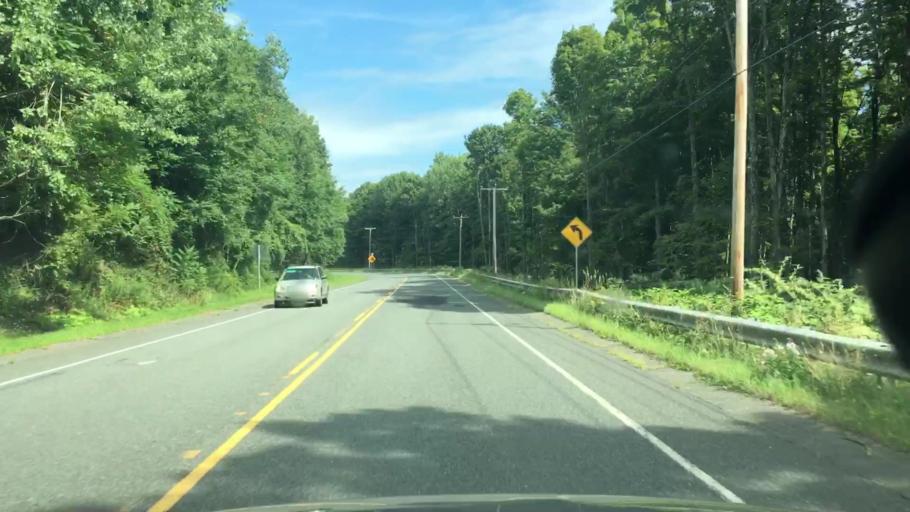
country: US
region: Massachusetts
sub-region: Franklin County
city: Colrain
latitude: 42.6626
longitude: -72.6816
